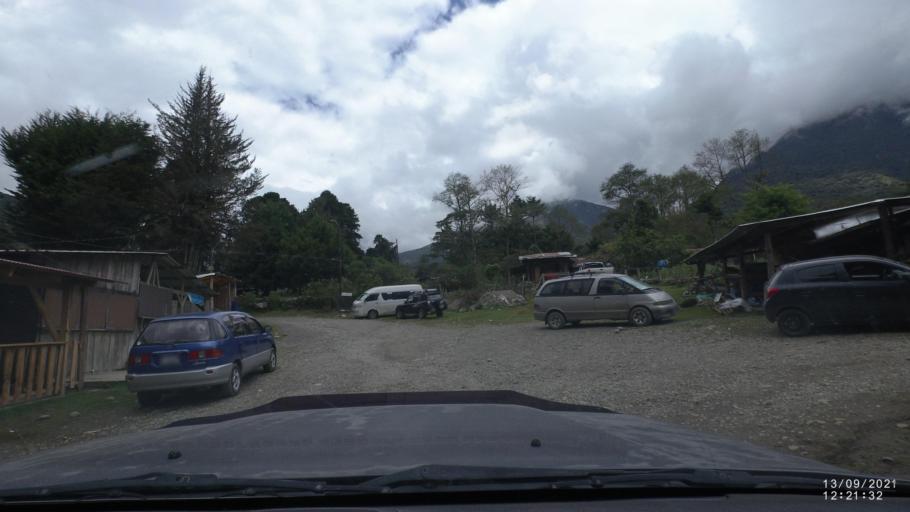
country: BO
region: Cochabamba
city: Colomi
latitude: -17.2368
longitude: -65.8172
